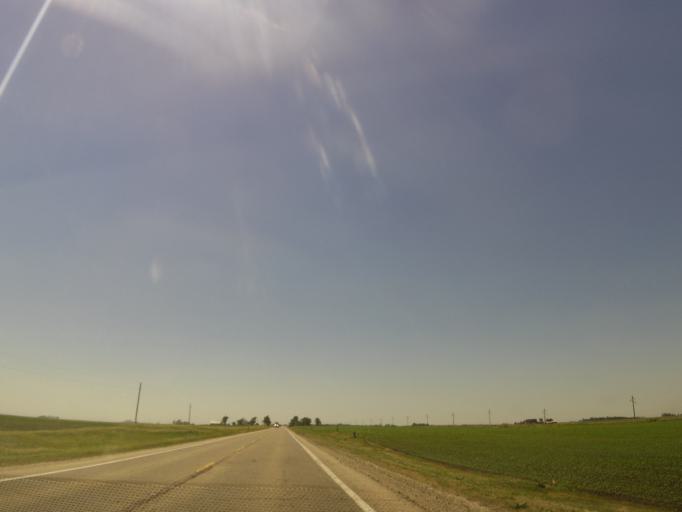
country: US
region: Illinois
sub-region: McLean County
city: Gridley
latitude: 40.7383
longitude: -88.9385
